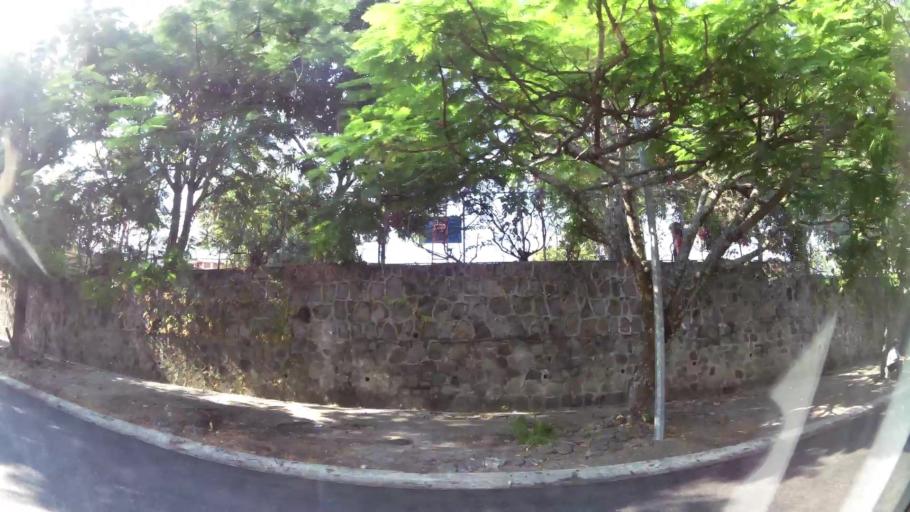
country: SV
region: La Libertad
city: Antiguo Cuscatlan
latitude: 13.6738
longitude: -89.2333
